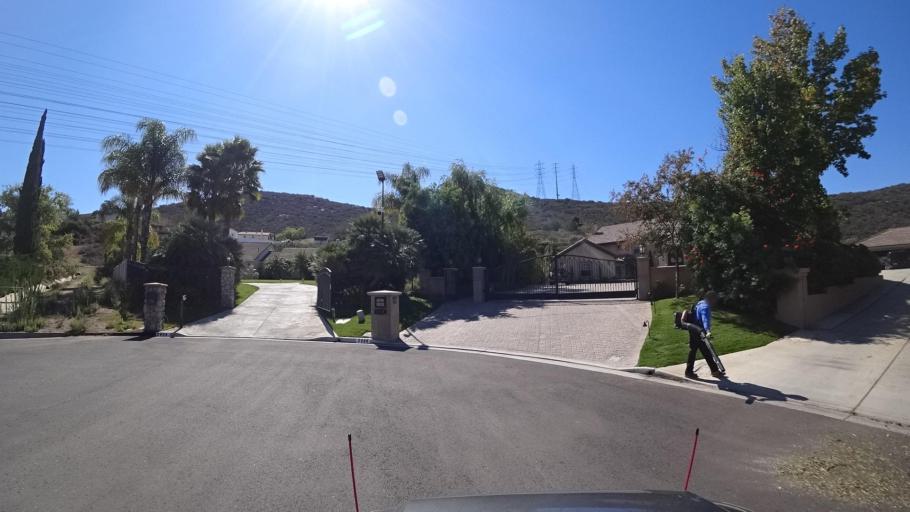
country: US
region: California
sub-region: San Diego County
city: Rancho San Diego
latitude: 32.7363
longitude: -116.9181
